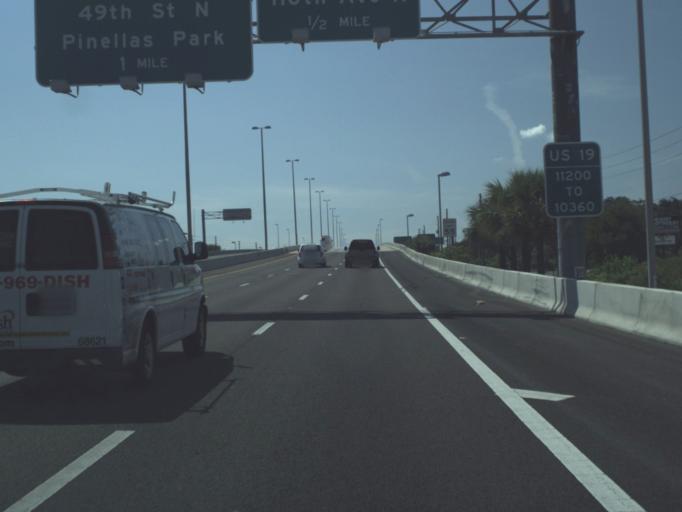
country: US
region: Florida
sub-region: Pinellas County
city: South Highpoint
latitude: 27.8820
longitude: -82.7143
